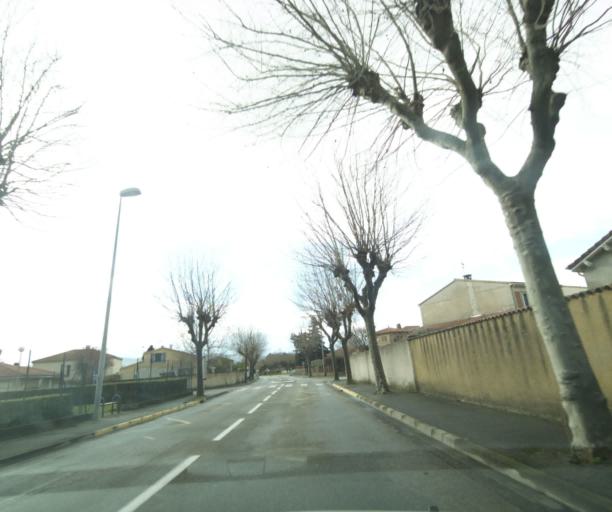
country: FR
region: Rhone-Alpes
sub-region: Departement de la Drome
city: Bourg-les-Valence
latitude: 44.9560
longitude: 4.9107
